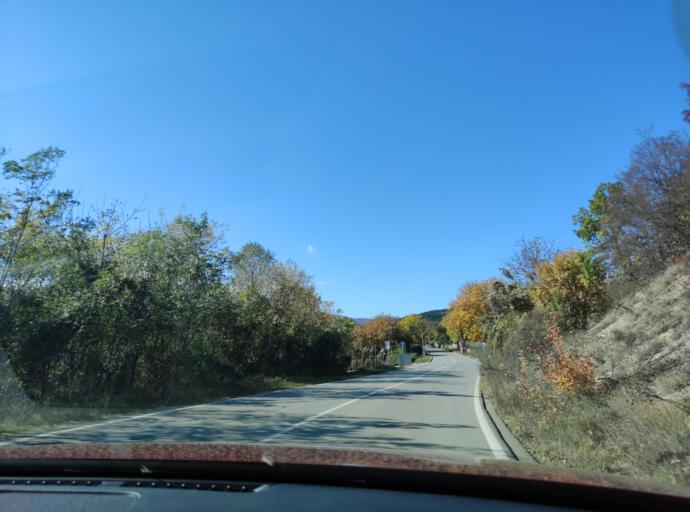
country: BG
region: Montana
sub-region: Obshtina Chiprovtsi
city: Chiprovtsi
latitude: 43.4325
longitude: 22.9824
